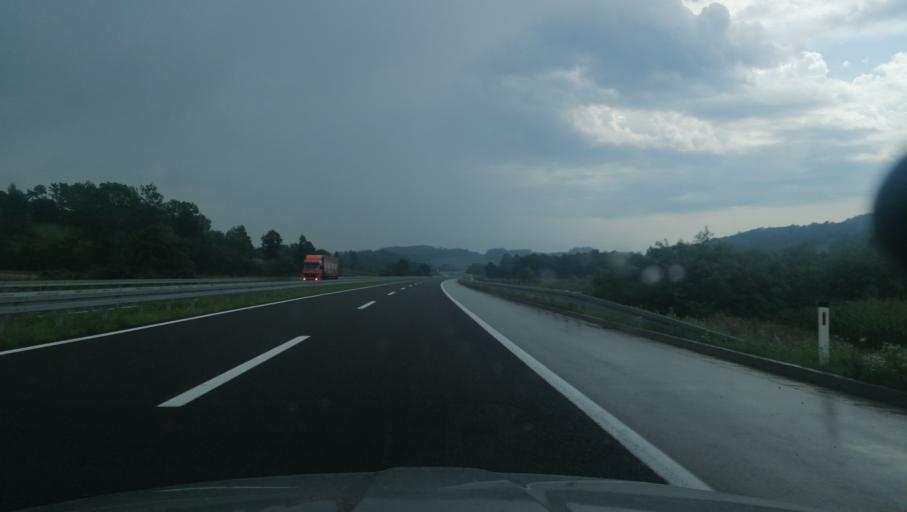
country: BA
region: Republika Srpska
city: Maglajani
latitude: 44.8715
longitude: 17.4147
